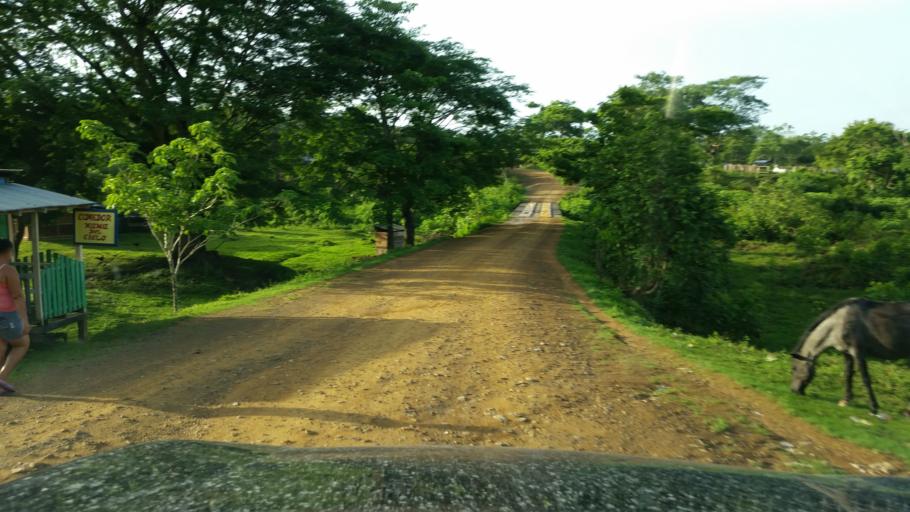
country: NI
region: Atlantico Norte (RAAN)
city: Puerto Cabezas
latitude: 14.0690
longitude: -83.9869
